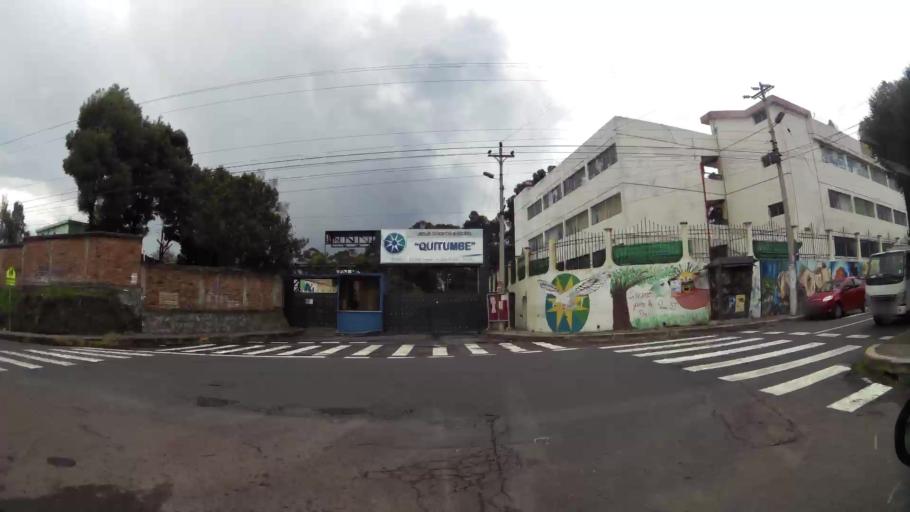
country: EC
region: Pichincha
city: Quito
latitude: -0.2835
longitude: -78.5497
